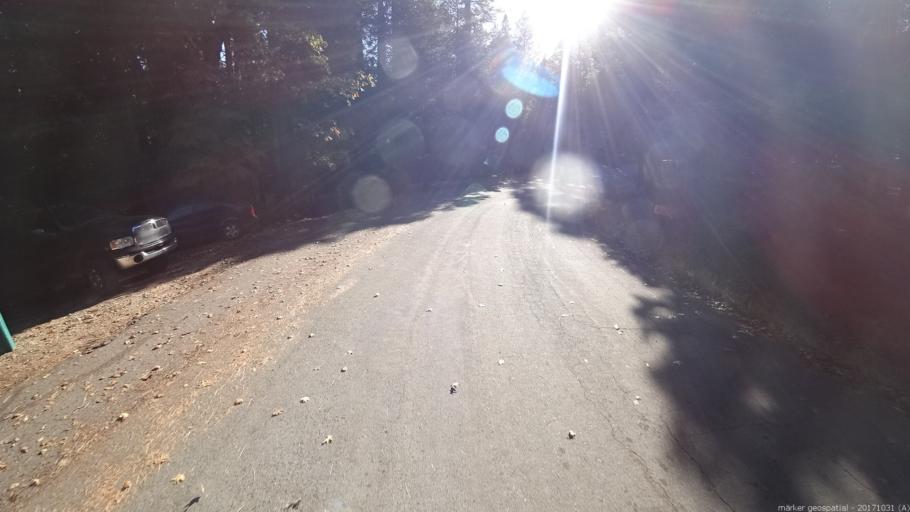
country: US
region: California
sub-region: Shasta County
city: Shingletown
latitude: 40.5017
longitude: -121.9059
